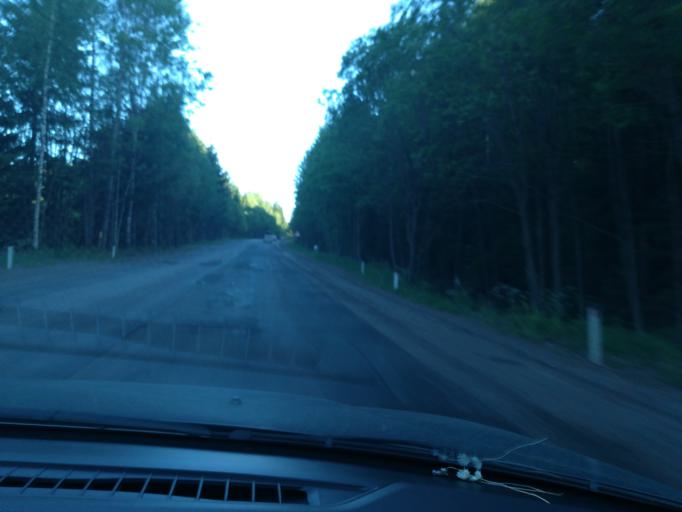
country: RU
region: Leningrad
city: Lesogorskiy
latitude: 60.9795
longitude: 28.9092
